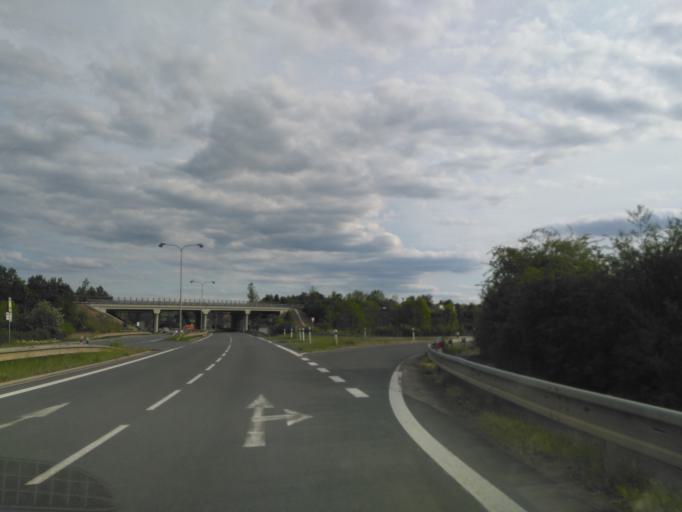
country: CZ
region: Central Bohemia
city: Zdice
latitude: 49.9035
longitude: 13.9611
